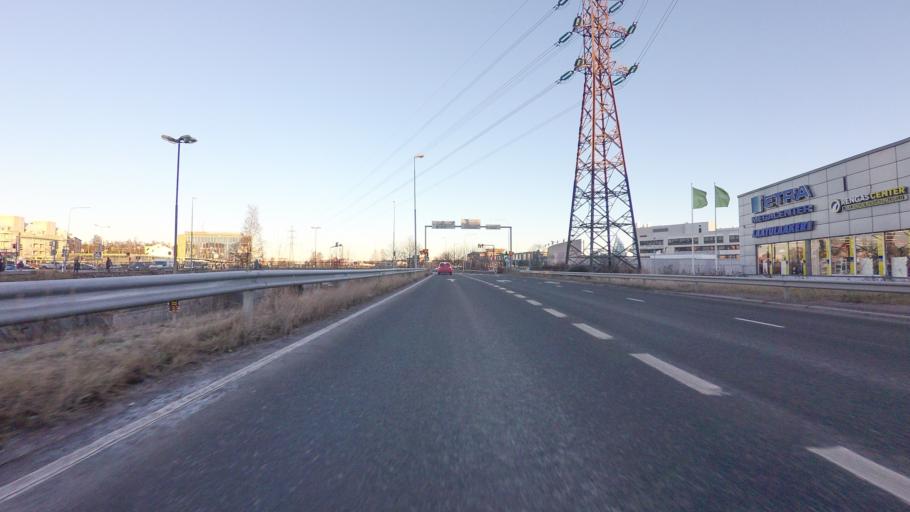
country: FI
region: Uusimaa
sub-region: Helsinki
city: Helsinki
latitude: 60.1935
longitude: 25.0299
